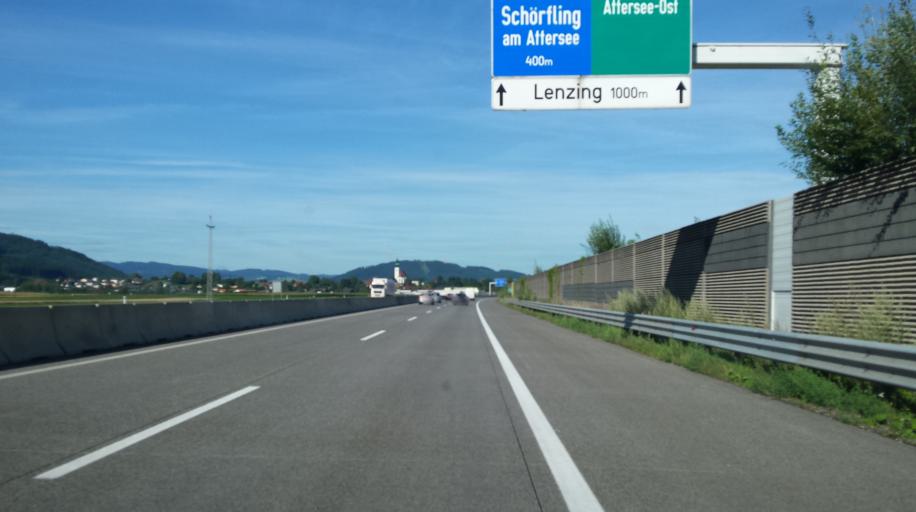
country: AT
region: Upper Austria
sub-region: Politischer Bezirk Vocklabruck
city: Lenzing
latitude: 47.9523
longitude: 13.6235
